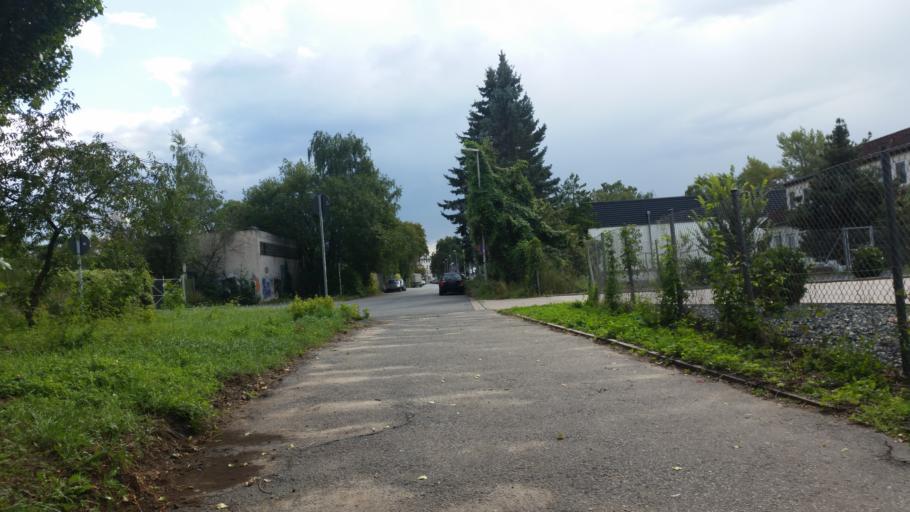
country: DE
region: Lower Saxony
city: Hannover
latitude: 52.4002
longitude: 9.7658
